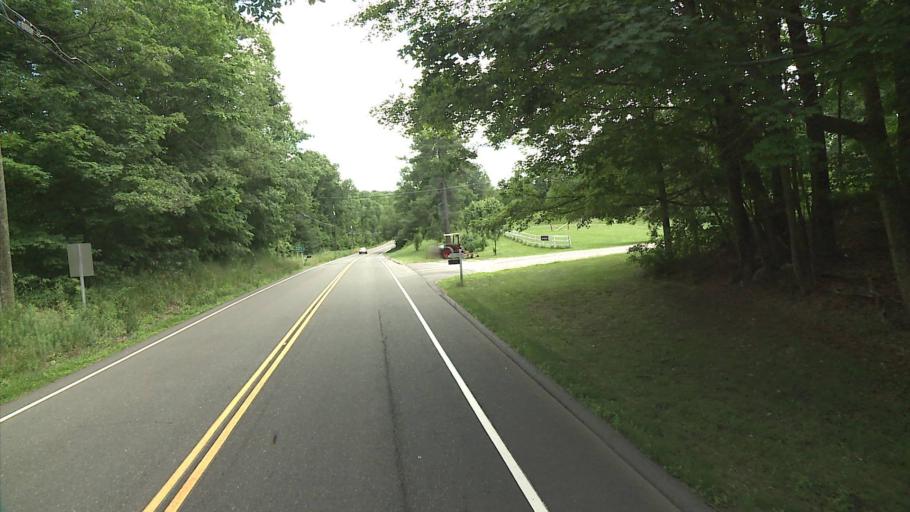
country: US
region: Connecticut
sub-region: Litchfield County
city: Bethlehem Village
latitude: 41.6697
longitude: -73.1673
